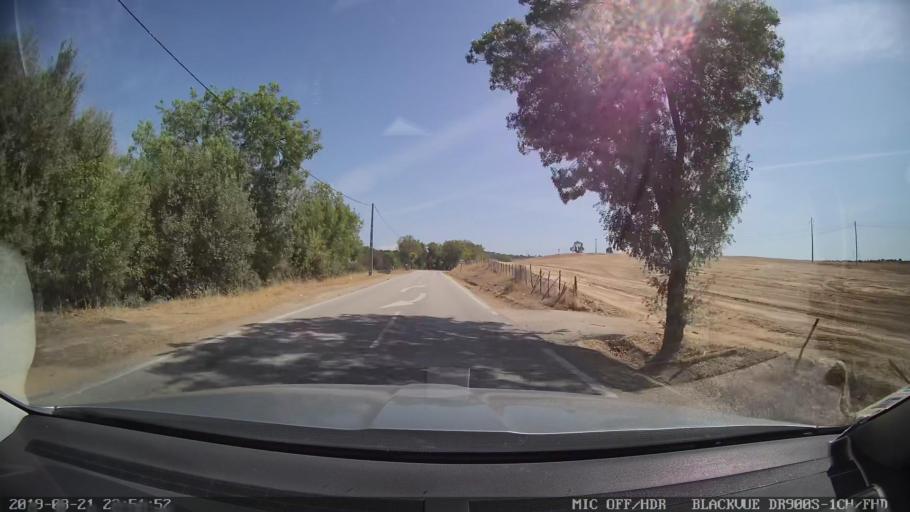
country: PT
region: Castelo Branco
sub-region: Idanha-A-Nova
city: Idanha-a-Nova
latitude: 39.9065
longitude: -7.2322
